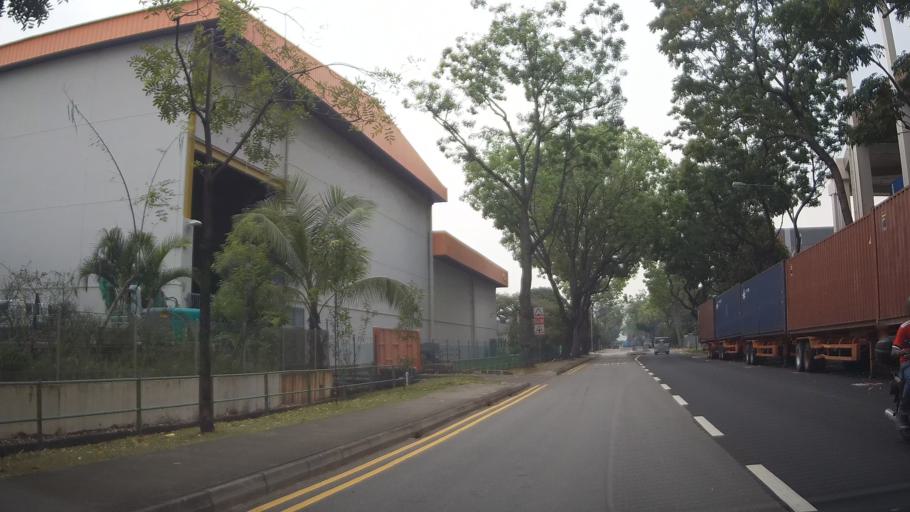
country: MY
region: Johor
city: Johor Bahru
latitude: 1.3151
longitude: 103.6718
